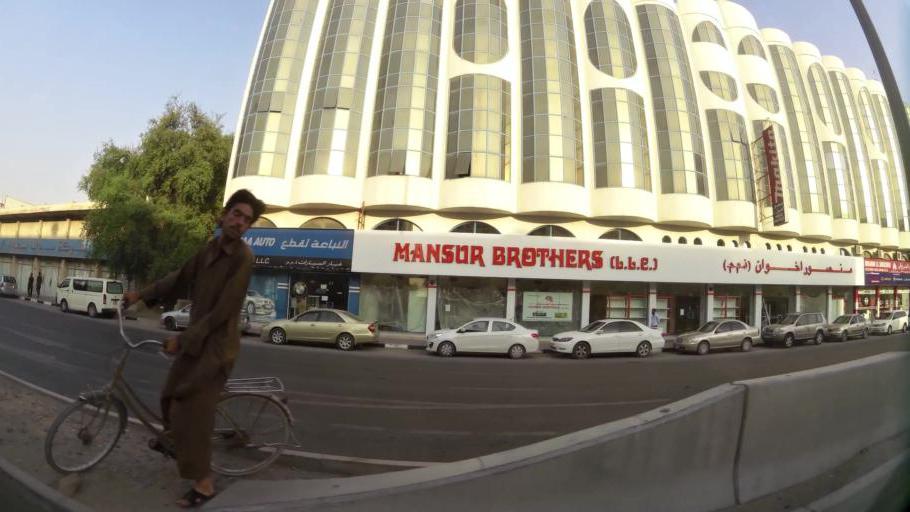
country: AE
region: Ash Shariqah
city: Sharjah
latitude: 25.3178
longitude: 55.3993
